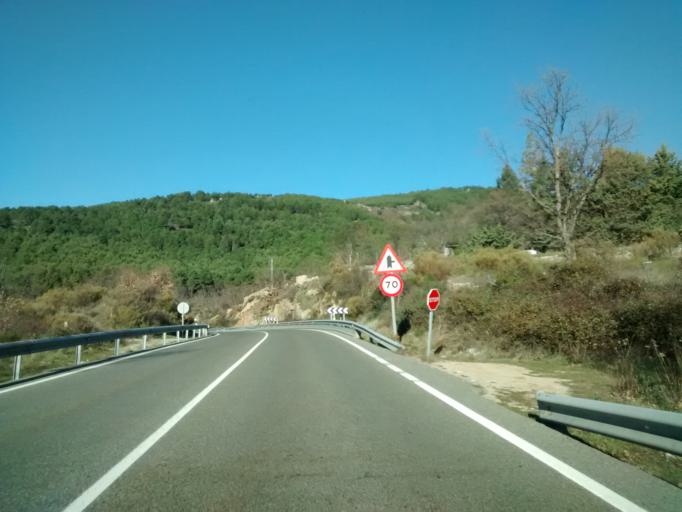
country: ES
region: Madrid
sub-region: Provincia de Madrid
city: Navacerrada
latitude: 40.7349
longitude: -4.0085
